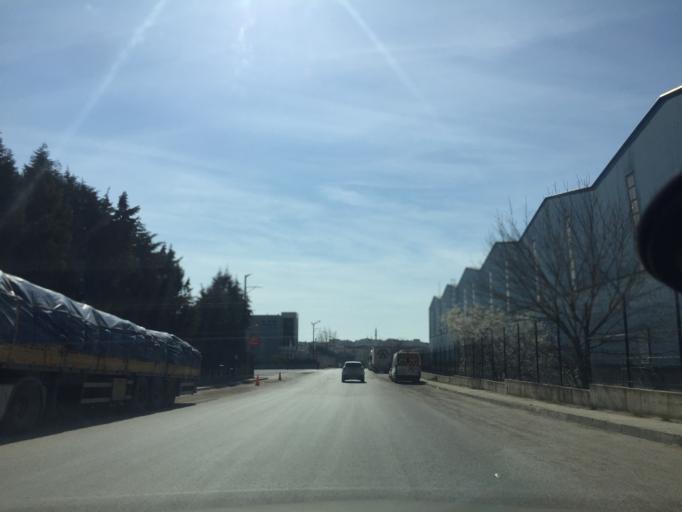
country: TR
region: Istanbul
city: Icmeler
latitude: 40.8385
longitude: 29.3163
